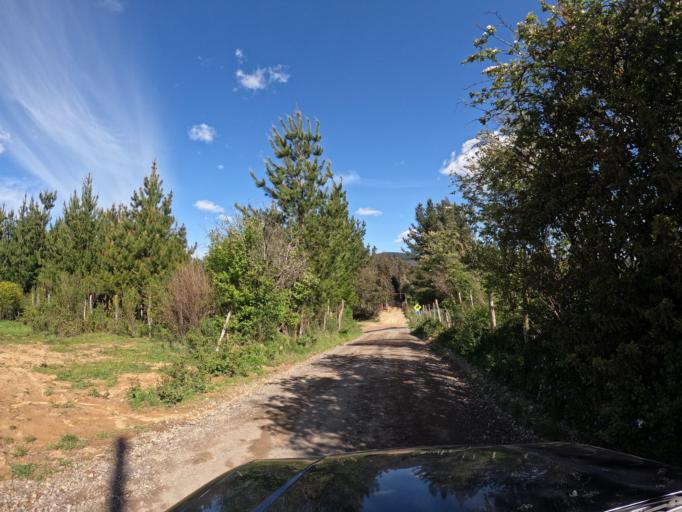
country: CL
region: Biobio
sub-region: Provincia de Concepcion
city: Chiguayante
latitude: -37.0636
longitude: -72.8889
